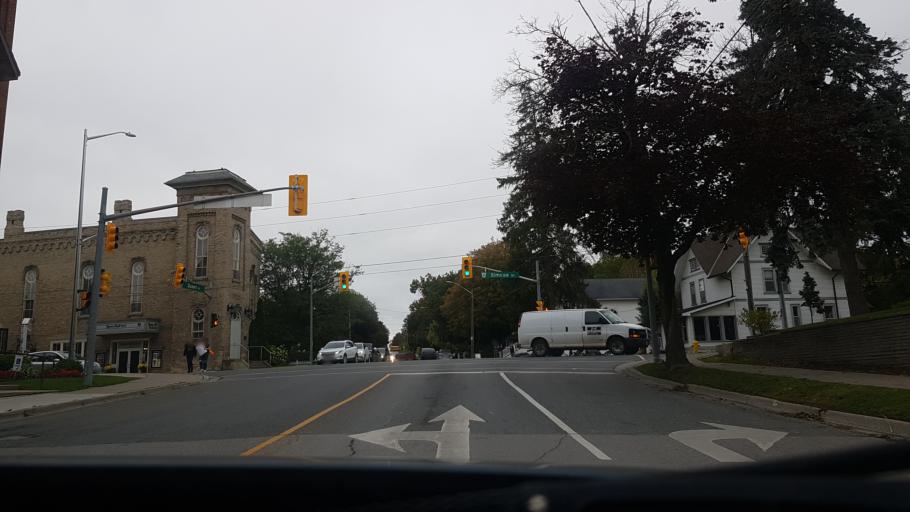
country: CA
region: Ontario
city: Uxbridge
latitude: 44.1038
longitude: -78.9470
